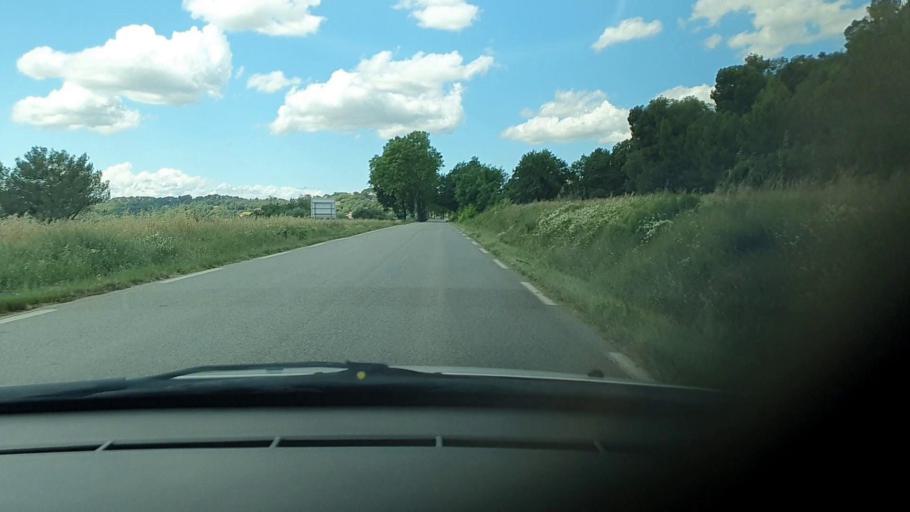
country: FR
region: Languedoc-Roussillon
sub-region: Departement du Gard
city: Montaren-et-Saint-Mediers
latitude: 44.0334
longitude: 4.3664
